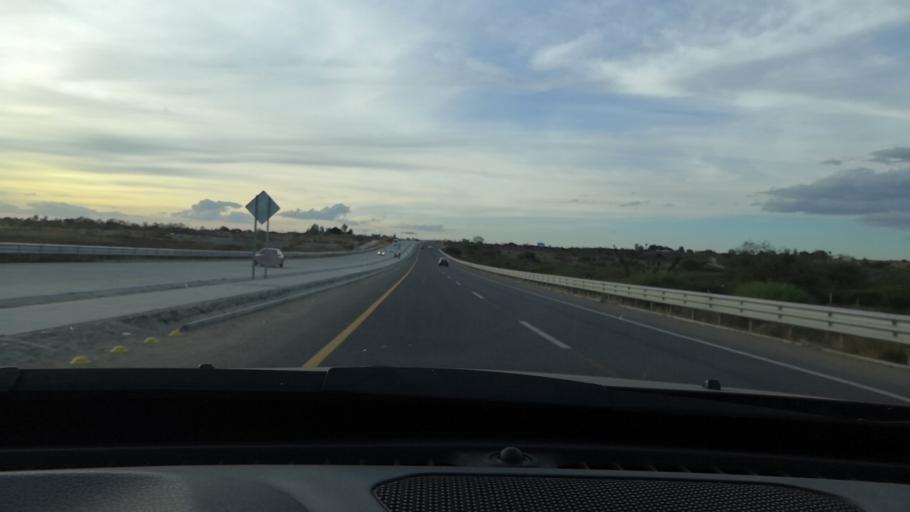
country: MX
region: Guanajuato
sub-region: Silao de la Victoria
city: El Refugio de los Sauces
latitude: 21.0341
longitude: -101.5071
